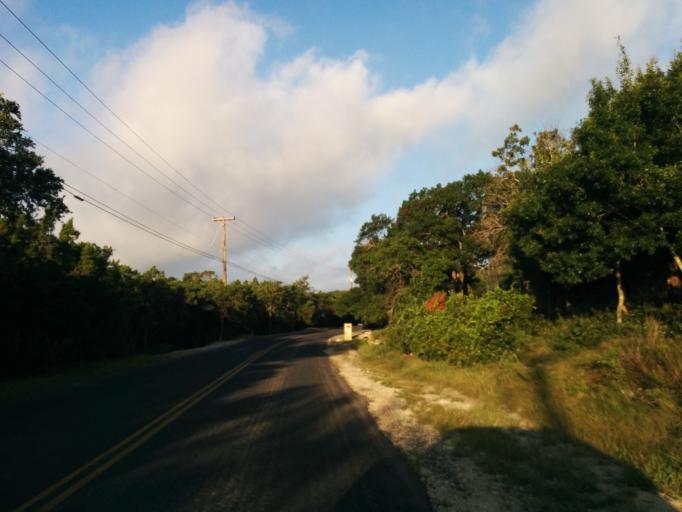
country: US
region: Texas
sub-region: Bexar County
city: Cross Mountain
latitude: 29.6556
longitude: -98.6352
